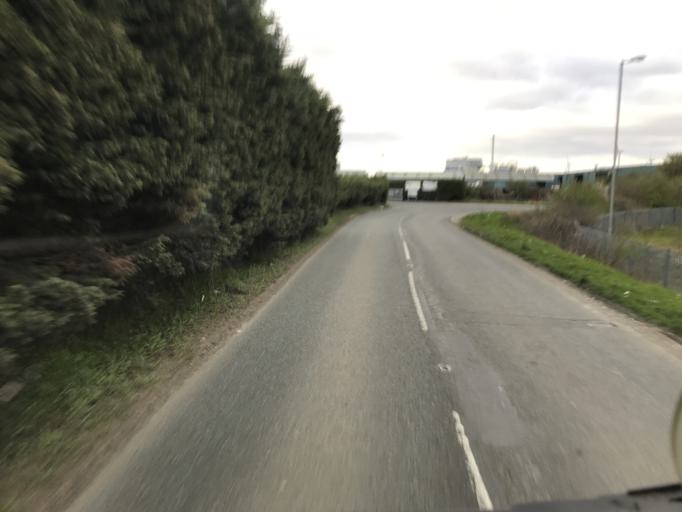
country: GB
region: England
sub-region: North Lincolnshire
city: Burton upon Stather
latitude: 53.6176
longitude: -0.6993
